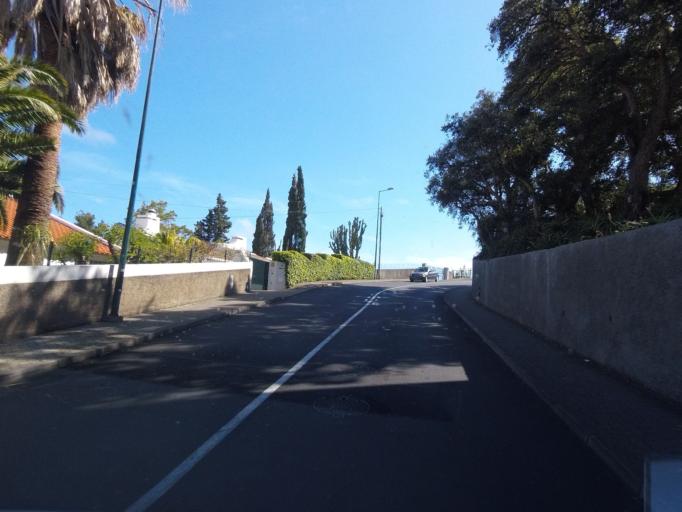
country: PT
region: Madeira
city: Canico
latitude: 32.6435
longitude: -16.8554
